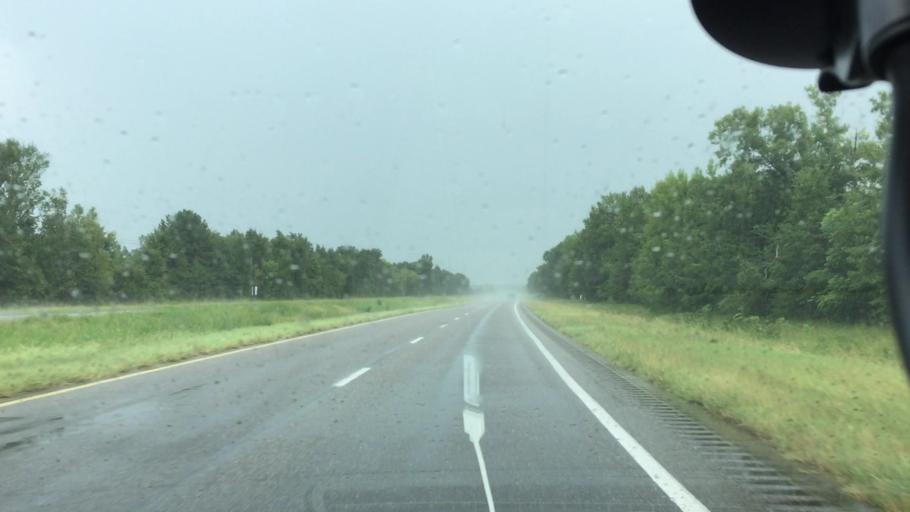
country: US
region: Alabama
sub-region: Montgomery County
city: Pike Road
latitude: 32.2421
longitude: -86.1332
